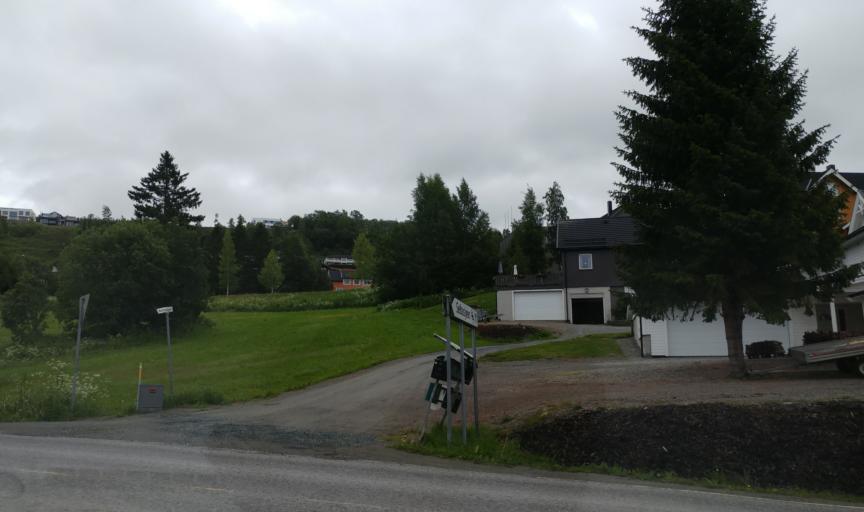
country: NO
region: Sor-Trondelag
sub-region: Selbu
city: Mebonden
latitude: 63.2319
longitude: 11.0340
